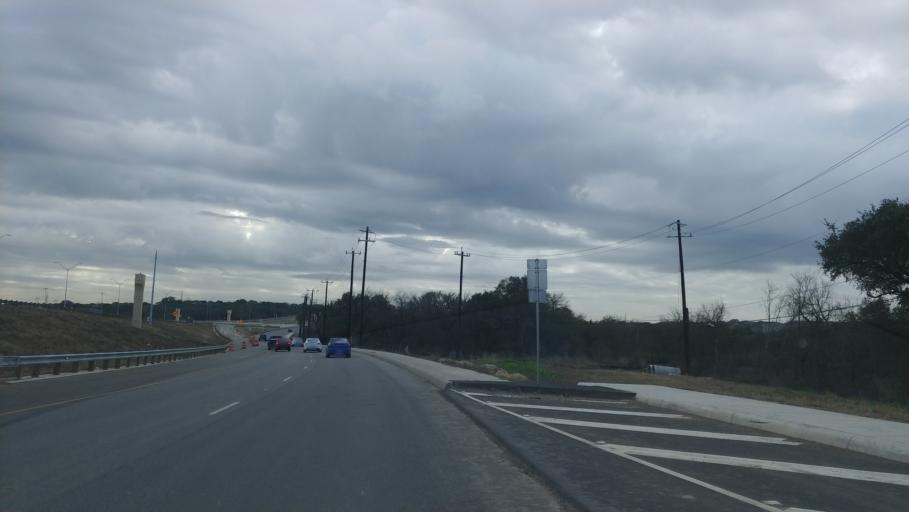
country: US
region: Texas
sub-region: Bexar County
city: Lackland Air Force Base
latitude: 29.4255
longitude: -98.7117
